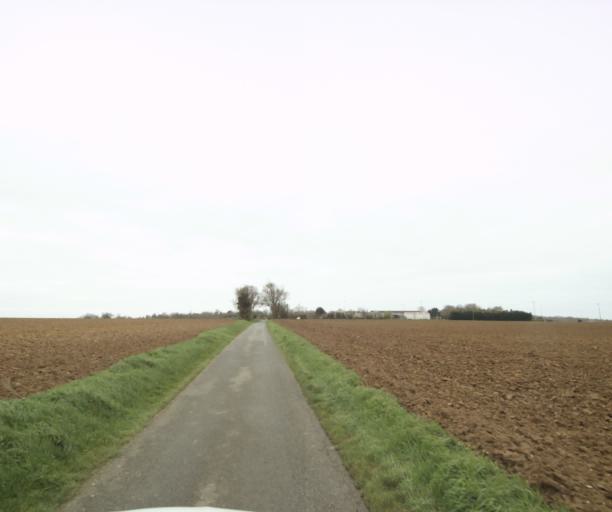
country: FR
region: Poitou-Charentes
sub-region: Departement de la Charente-Maritime
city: Nieul-sur-Mer
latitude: 46.1939
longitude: -1.1660
